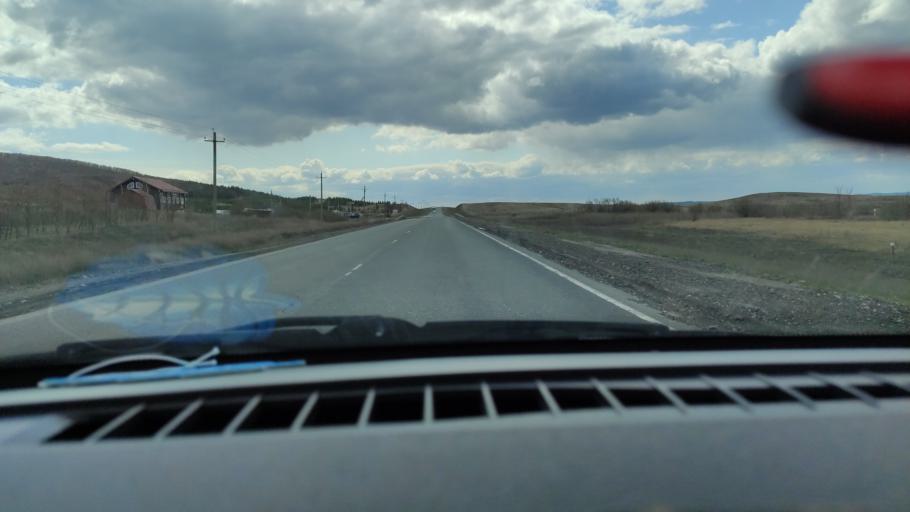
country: RU
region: Saratov
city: Alekseyevka
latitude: 52.3037
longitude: 47.9264
